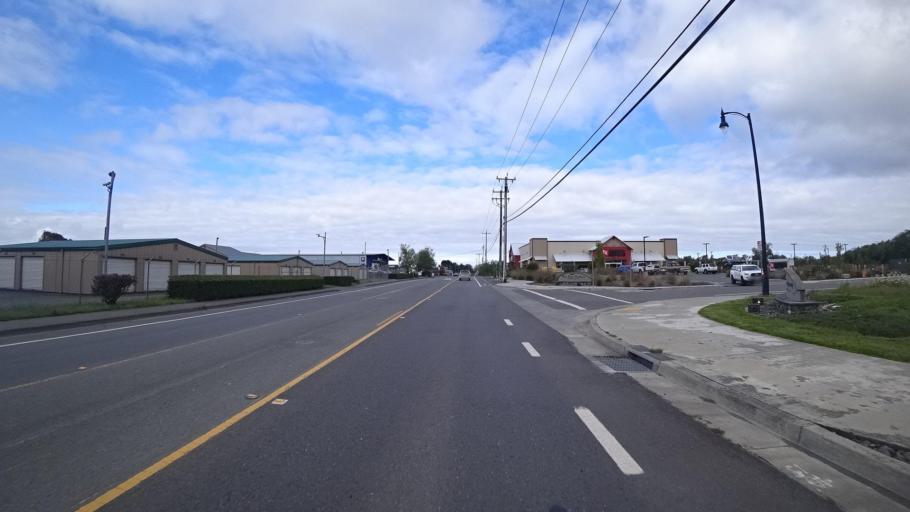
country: US
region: California
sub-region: Humboldt County
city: Arcata
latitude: 40.9050
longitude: -124.0793
